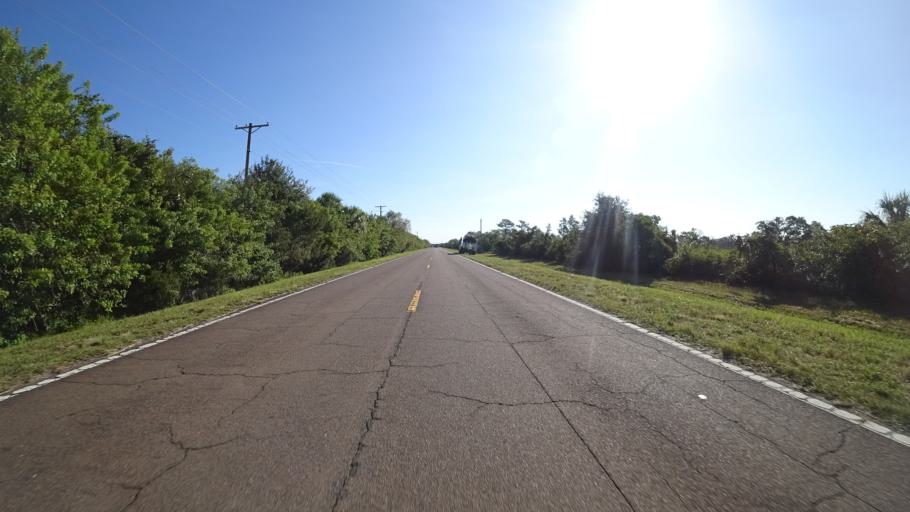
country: US
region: Florida
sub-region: Hillsborough County
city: Ruskin
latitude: 27.6540
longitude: -82.4632
